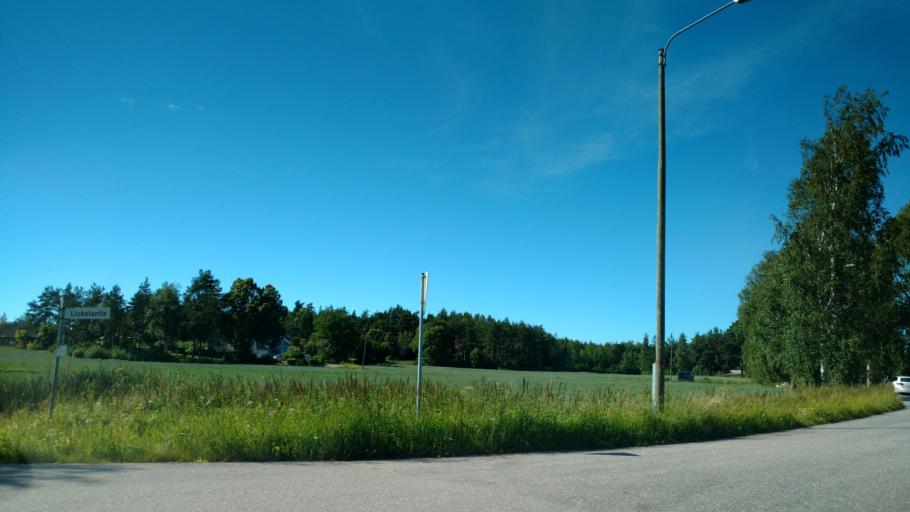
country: FI
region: Varsinais-Suomi
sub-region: Turku
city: Rusko
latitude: 60.5329
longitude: 22.2014
